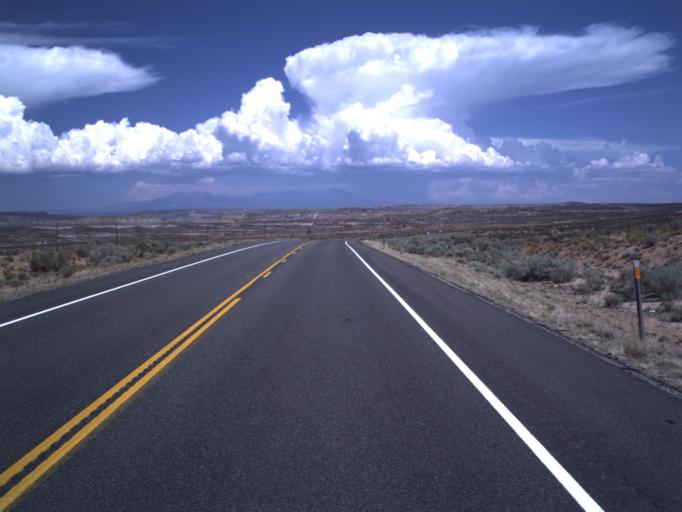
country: US
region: Utah
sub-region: San Juan County
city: Blanding
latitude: 37.3513
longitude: -109.5186
